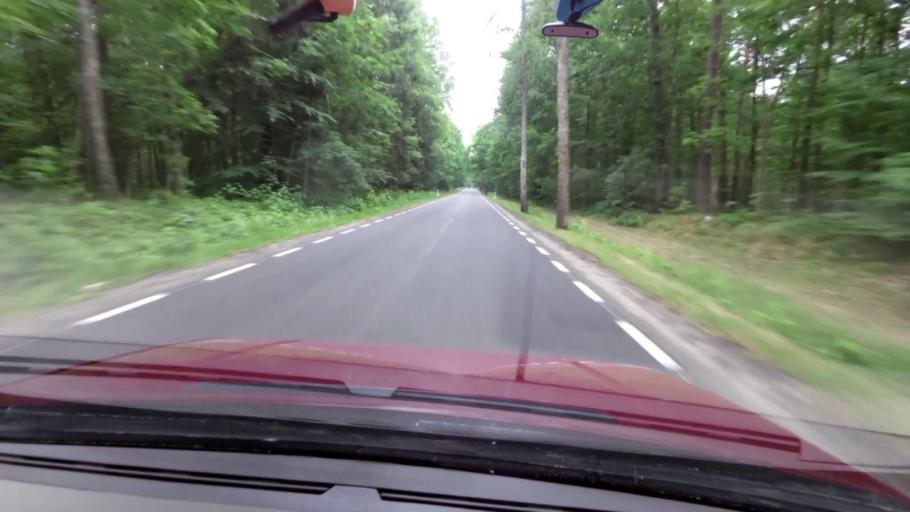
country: PL
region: Pomeranian Voivodeship
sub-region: Powiat slupski
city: Kepice
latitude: 54.2322
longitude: 16.8877
